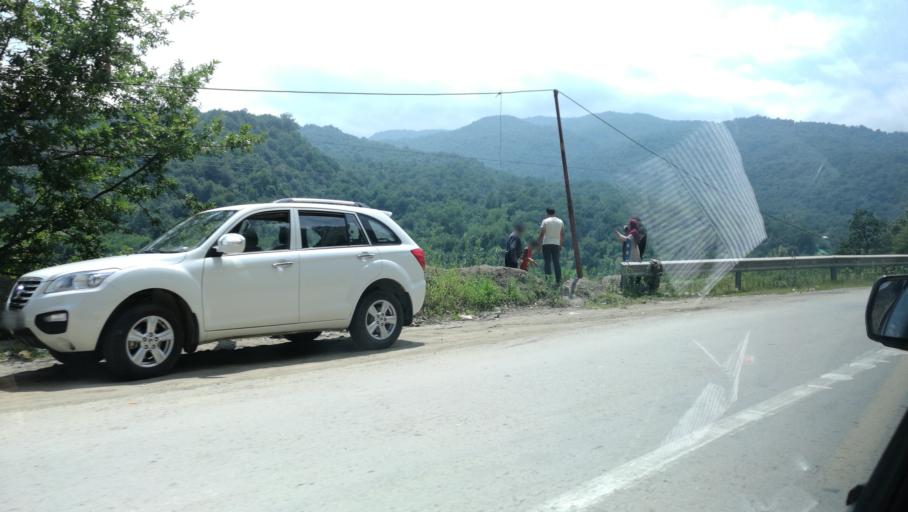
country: IR
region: Mazandaran
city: Ramsar
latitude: 36.9028
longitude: 50.5979
